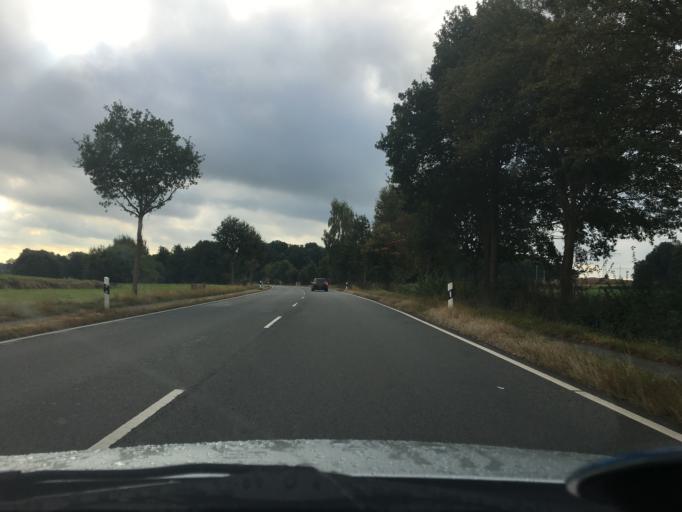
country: DE
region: Lower Saxony
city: Alfhausen
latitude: 52.5242
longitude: 7.9395
